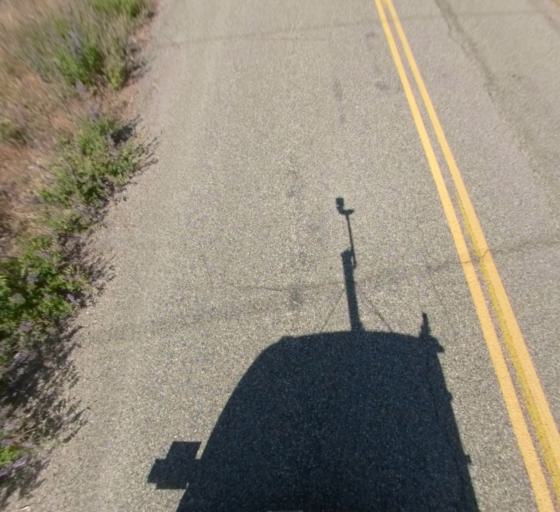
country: US
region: California
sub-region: Fresno County
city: Auberry
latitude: 37.3095
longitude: -119.3492
